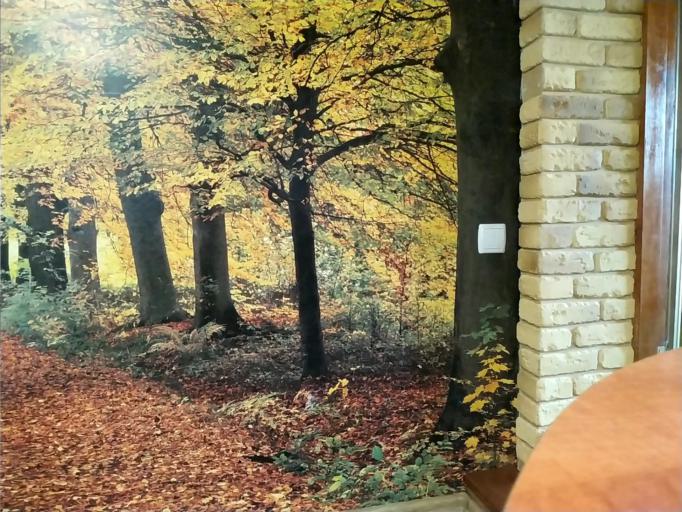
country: RU
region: Leningrad
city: Tolmachevo
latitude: 58.9322
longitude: 29.7105
